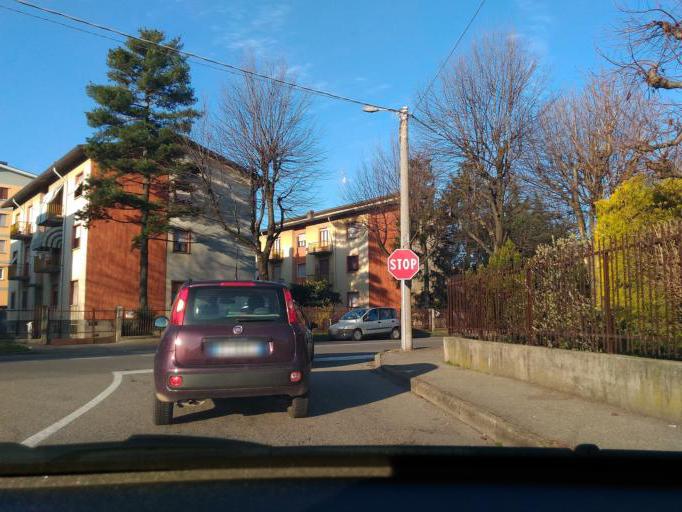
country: IT
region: Lombardy
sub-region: Provincia di Varese
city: Busto Arsizio
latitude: 45.6243
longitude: 8.8298
